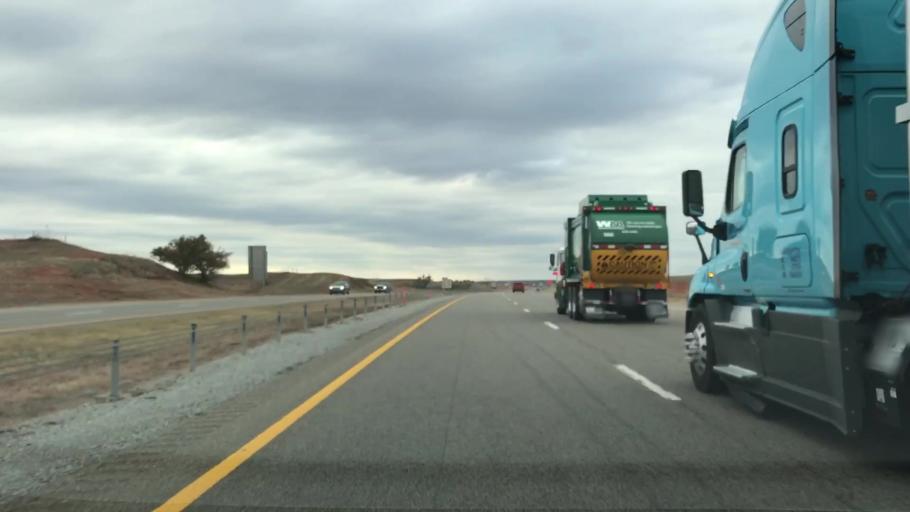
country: US
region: Oklahoma
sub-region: Washita County
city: Burns Flat
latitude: 35.4423
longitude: -99.1754
